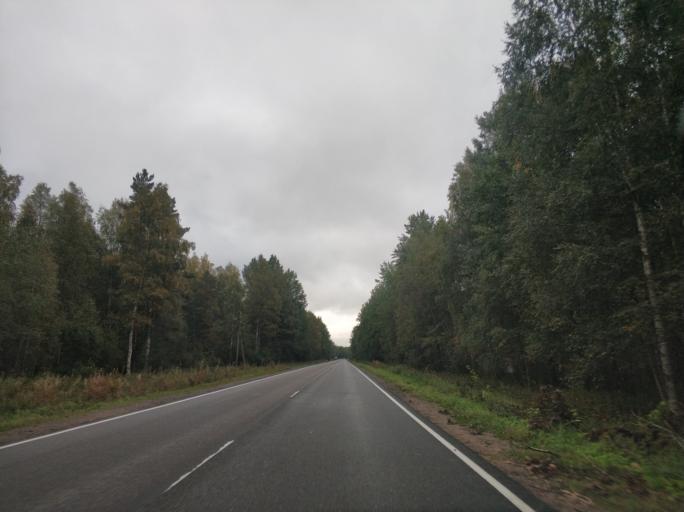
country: RU
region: Leningrad
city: Borisova Griva
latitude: 60.1229
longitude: 30.9634
